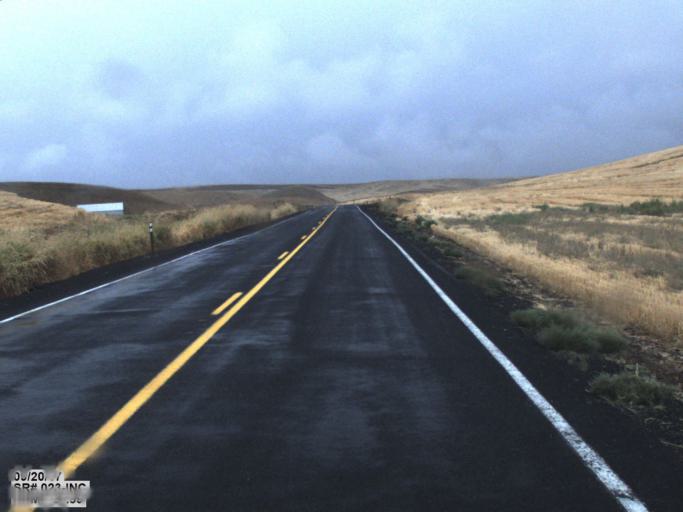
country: US
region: Washington
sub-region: Spokane County
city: Cheney
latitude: 47.1490
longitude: -117.8384
